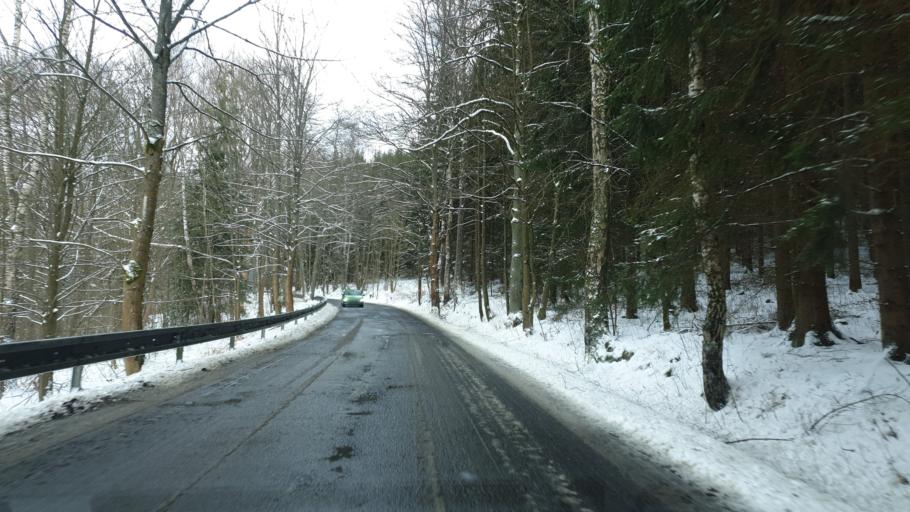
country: DE
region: Saxony
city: Bad Elster
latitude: 50.2680
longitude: 12.2487
